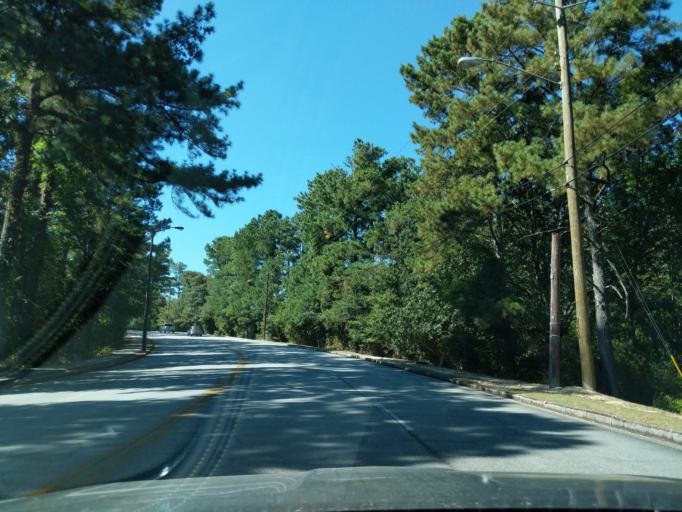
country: US
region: Georgia
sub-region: DeKalb County
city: Stone Mountain
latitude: 33.8127
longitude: -84.1388
